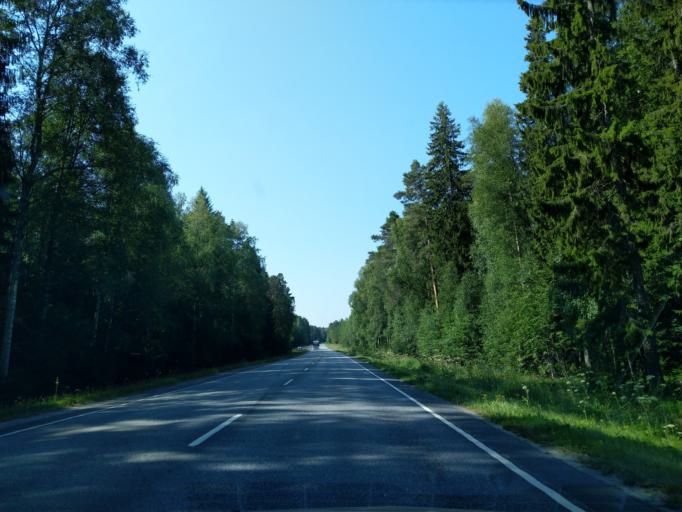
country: FI
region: Satakunta
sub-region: Pori
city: Noormarkku
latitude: 61.6073
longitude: 21.8830
